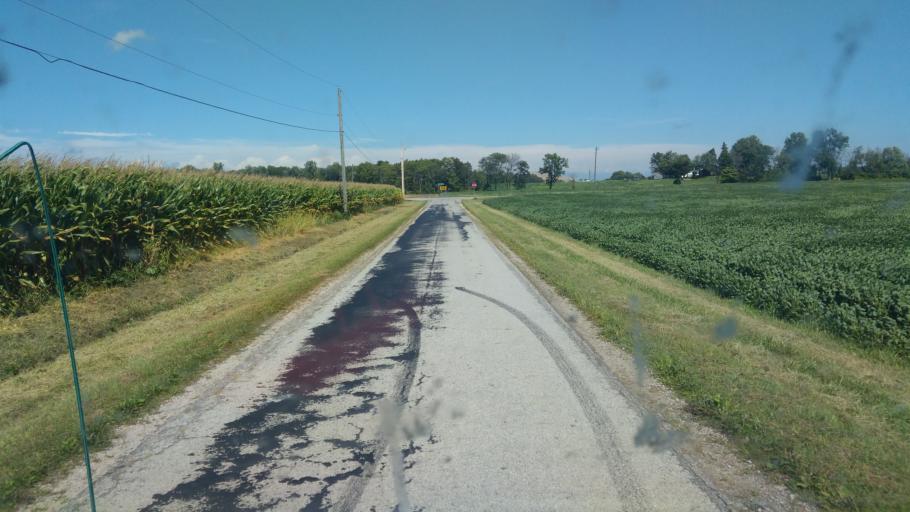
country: US
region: Ohio
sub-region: Crawford County
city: Bucyrus
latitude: 40.7973
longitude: -82.8731
